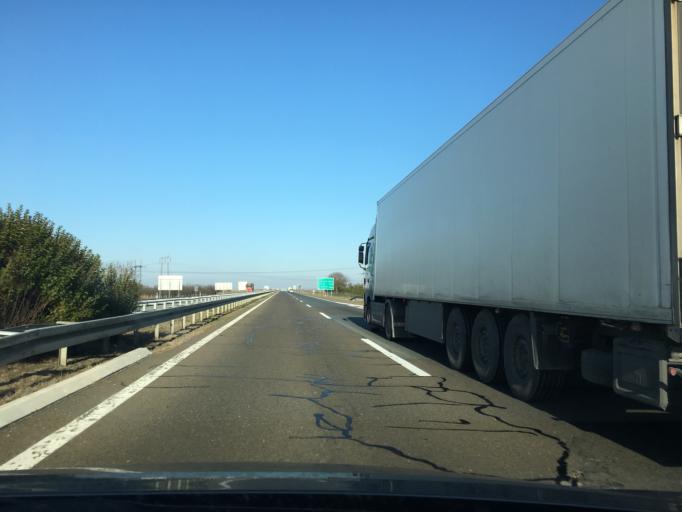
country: RS
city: Novi Karlovci
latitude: 45.0730
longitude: 20.1479
